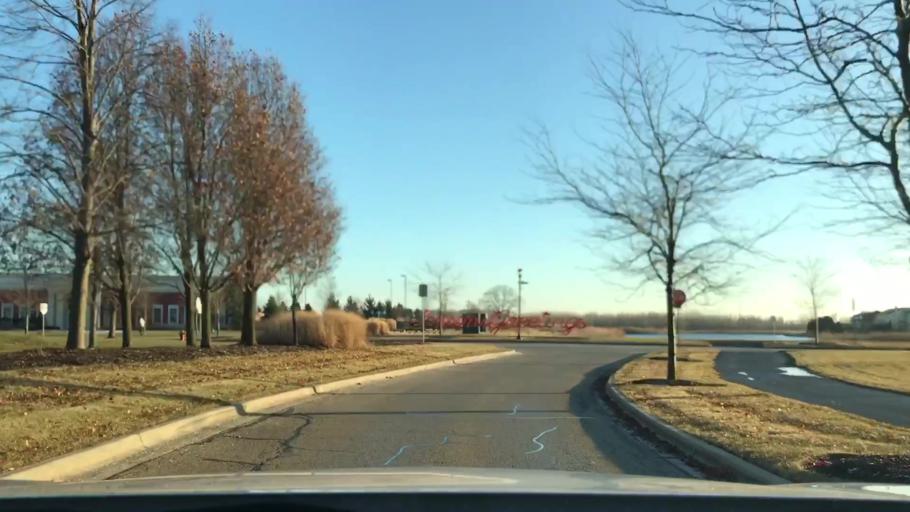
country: US
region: Illinois
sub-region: Kane County
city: Pingree Grove
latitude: 42.0862
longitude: -88.4362
